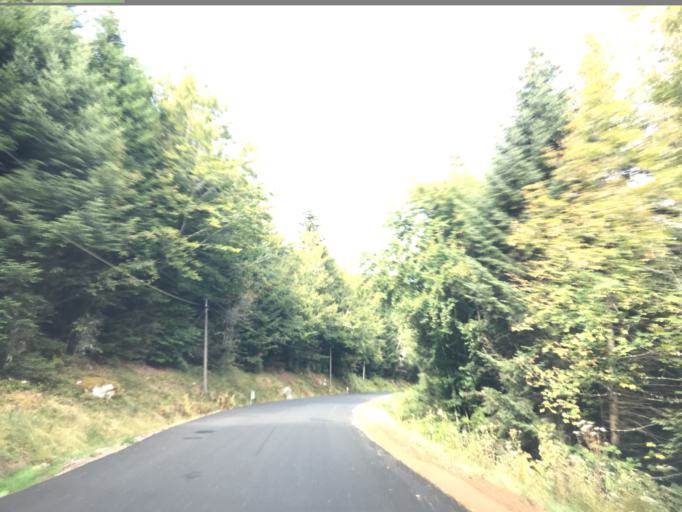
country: FR
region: Auvergne
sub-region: Departement du Puy-de-Dome
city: Celles-sur-Durolle
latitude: 45.8083
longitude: 3.6647
